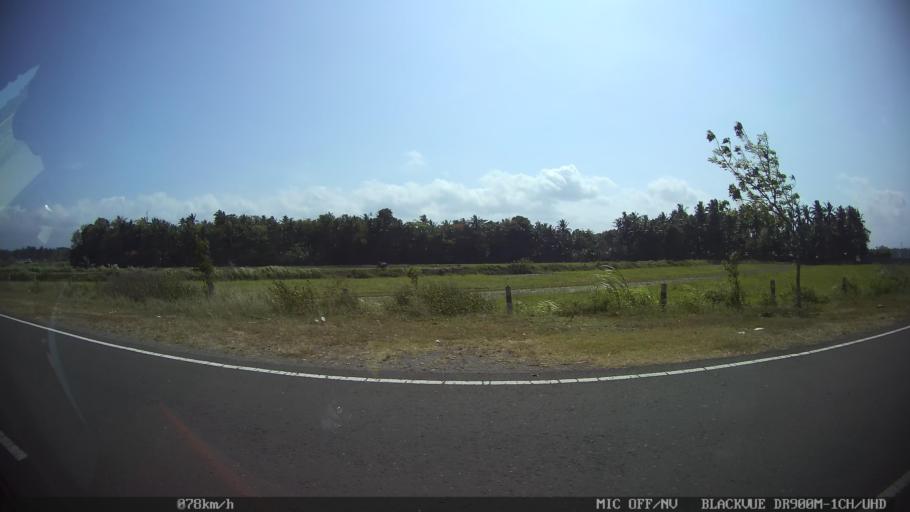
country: ID
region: Daerah Istimewa Yogyakarta
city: Srandakan
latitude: -7.9584
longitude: 110.2017
